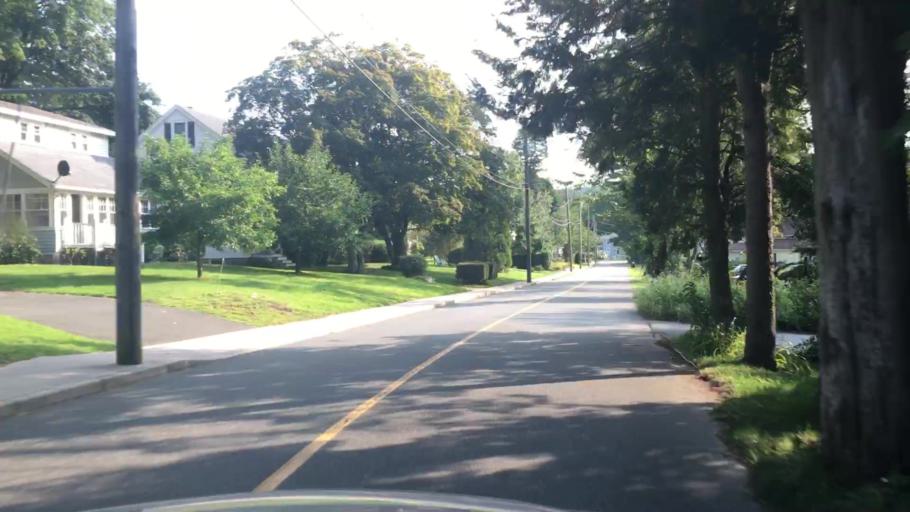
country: US
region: Connecticut
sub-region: Middlesex County
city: Deep River Center
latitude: 41.3854
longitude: -72.4325
